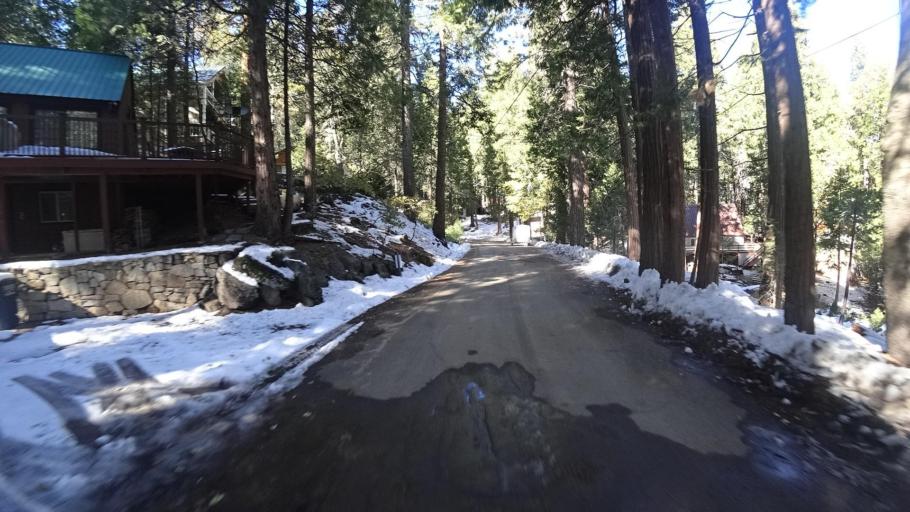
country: US
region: California
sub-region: Kern County
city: Alta Sierra
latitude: 35.7265
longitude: -118.5508
